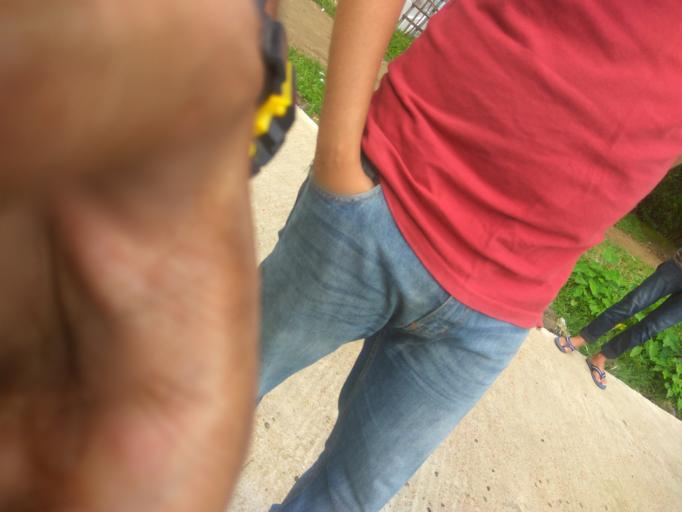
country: IN
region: Assam
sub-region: Karimganj
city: Karimganj
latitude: 24.8587
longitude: 92.1890
